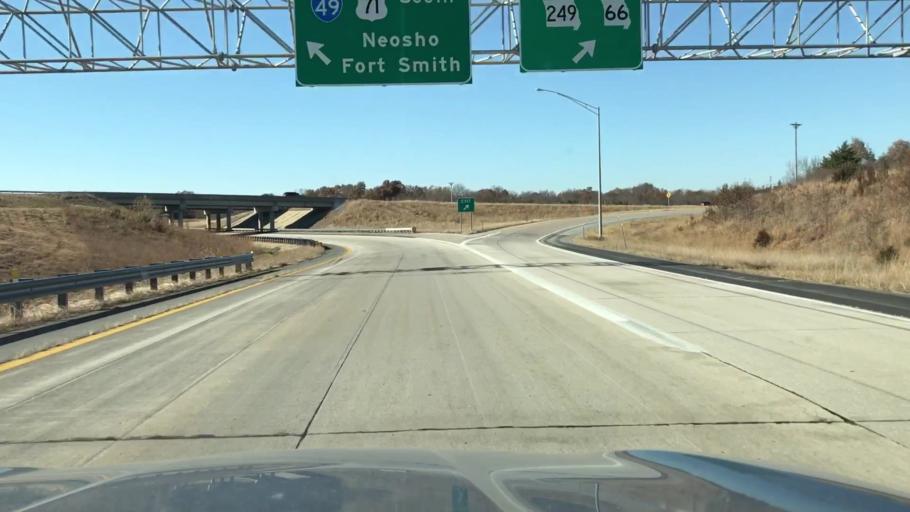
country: US
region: Missouri
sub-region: Jasper County
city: Duenweg
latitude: 37.0642
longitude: -94.4250
